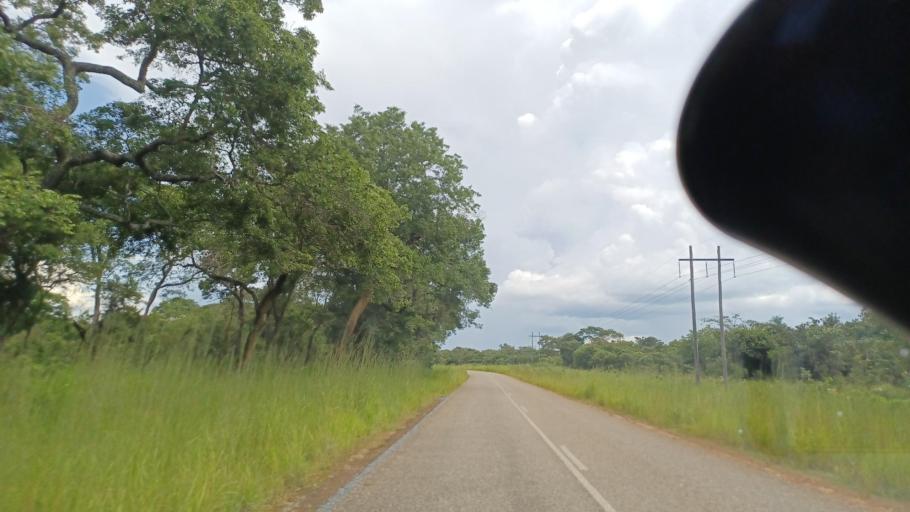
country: ZM
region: North-Western
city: Kasempa
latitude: -13.1515
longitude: 25.8777
